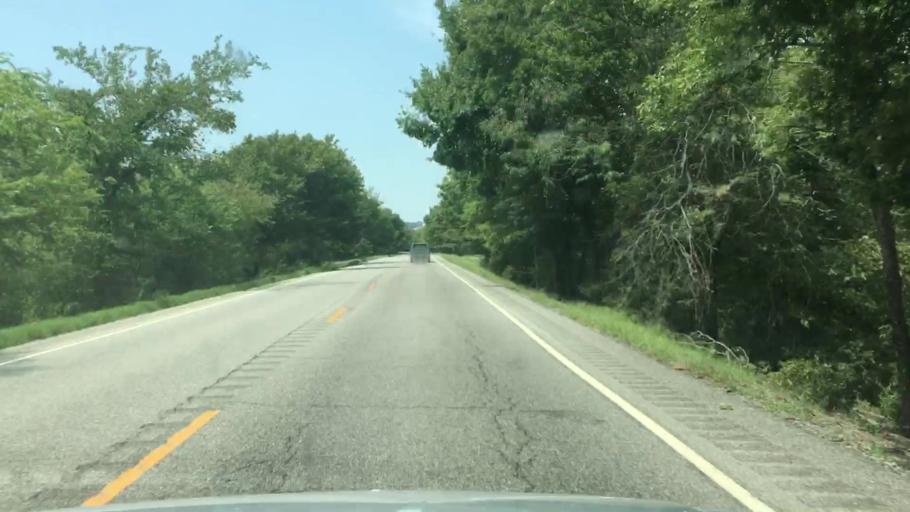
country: US
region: Oklahoma
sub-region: Muskogee County
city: Fort Gibson
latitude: 35.9369
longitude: -95.2173
